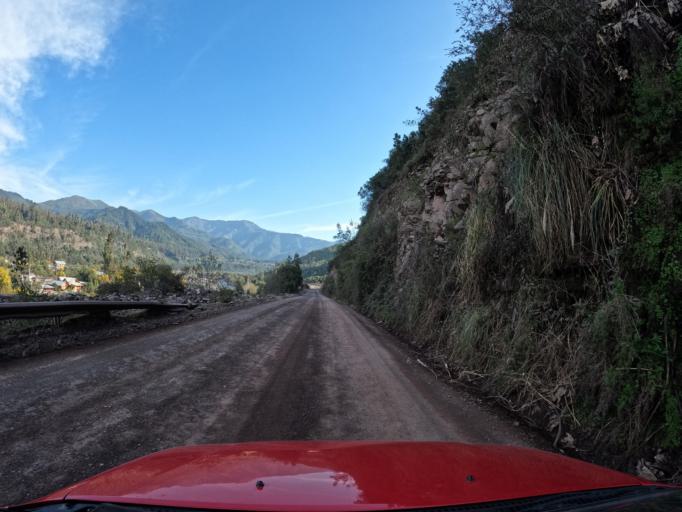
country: CL
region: O'Higgins
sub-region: Provincia de Colchagua
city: Chimbarongo
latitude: -34.9966
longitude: -70.8228
